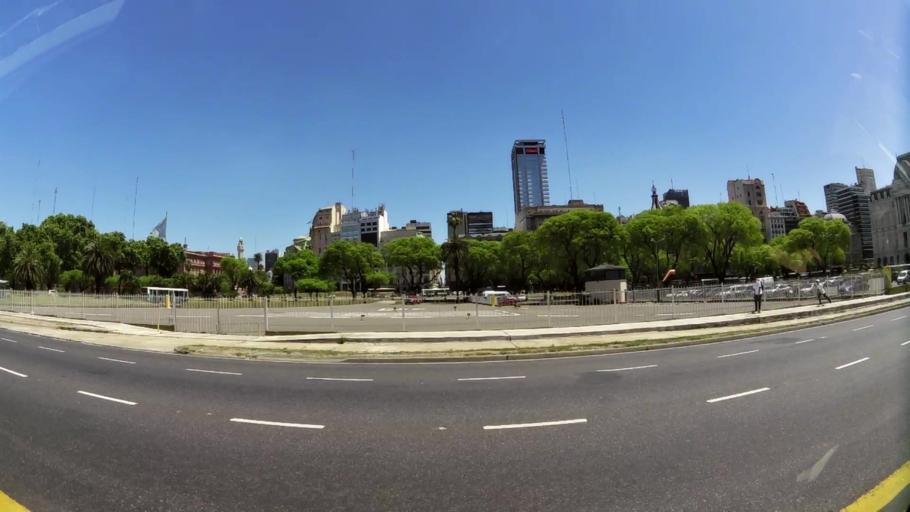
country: AR
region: Buenos Aires F.D.
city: Buenos Aires
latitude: -34.6063
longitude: -58.3678
